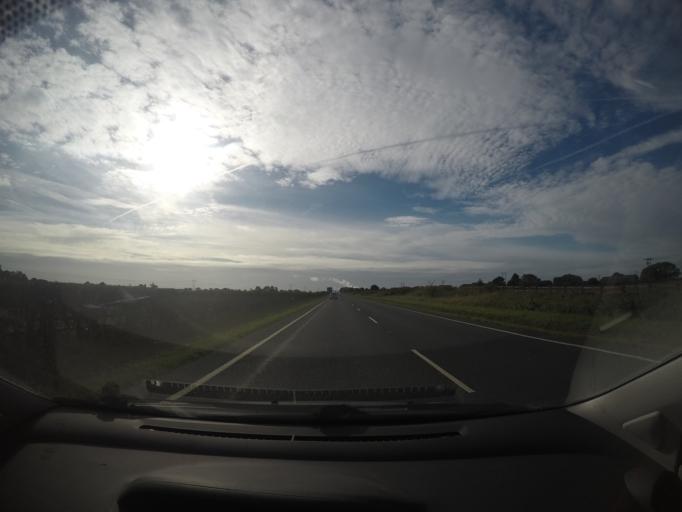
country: GB
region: England
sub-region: North Yorkshire
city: Barlby
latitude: 53.8137
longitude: -1.0413
